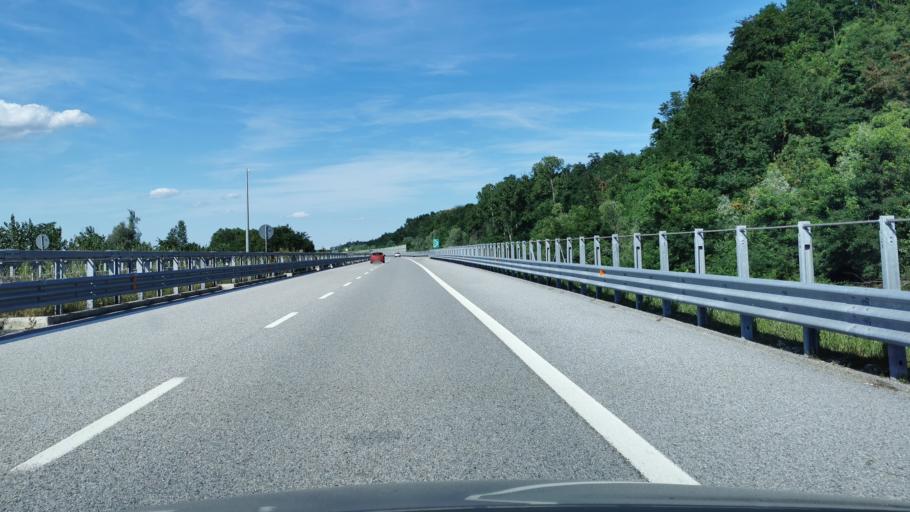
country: IT
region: Piedmont
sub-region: Provincia di Cuneo
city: Montanera
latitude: 44.4585
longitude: 7.6569
